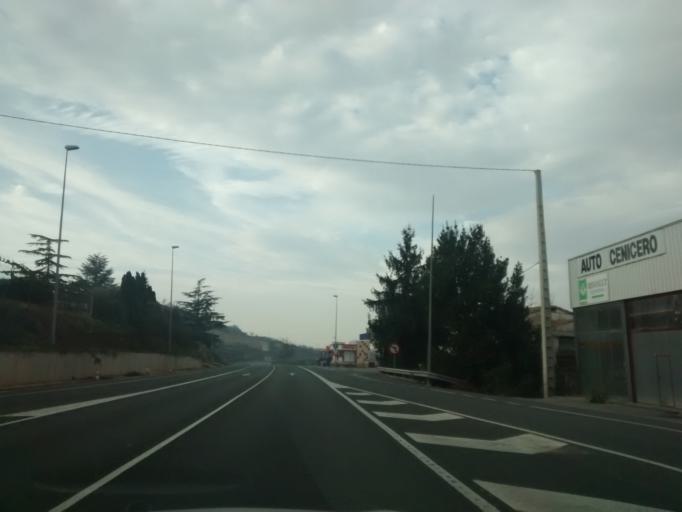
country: ES
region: La Rioja
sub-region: Provincia de La Rioja
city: Cenicero
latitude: 42.4827
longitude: -2.6516
